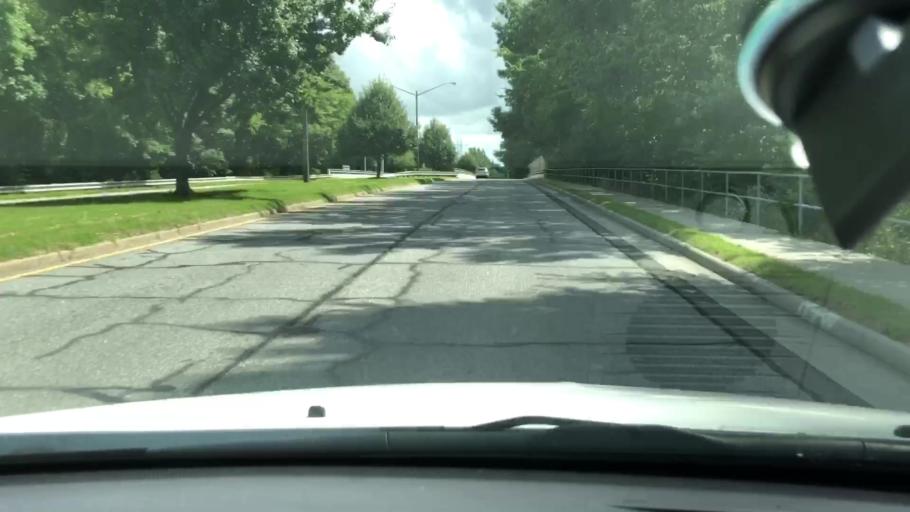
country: US
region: Virginia
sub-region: City of Chesapeake
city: Chesapeake
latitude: 36.8132
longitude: -76.1963
